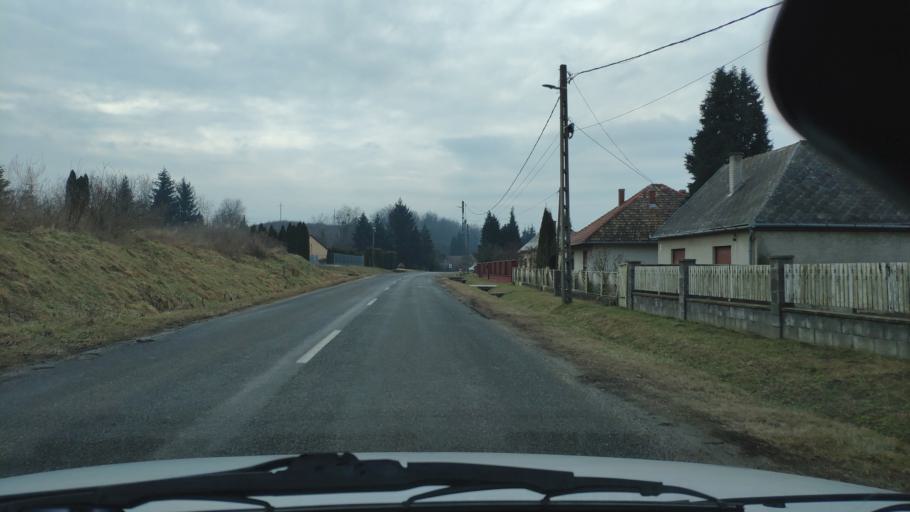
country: HU
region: Zala
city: Nagykanizsa
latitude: 46.5196
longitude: 16.9821
